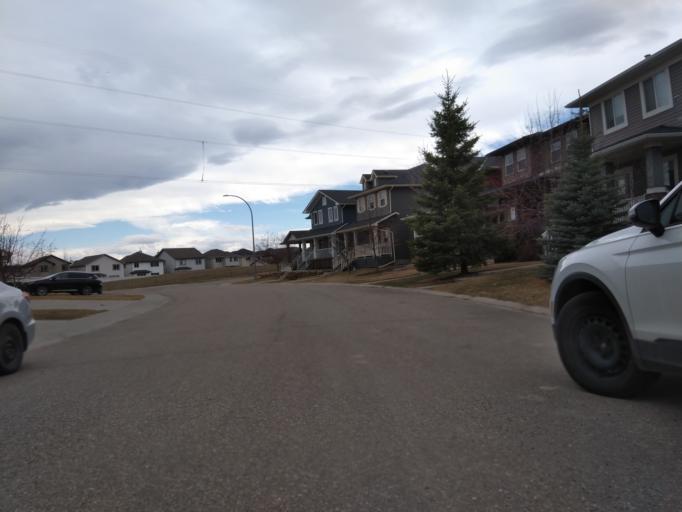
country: CA
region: Alberta
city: Calgary
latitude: 51.1694
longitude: -114.1085
